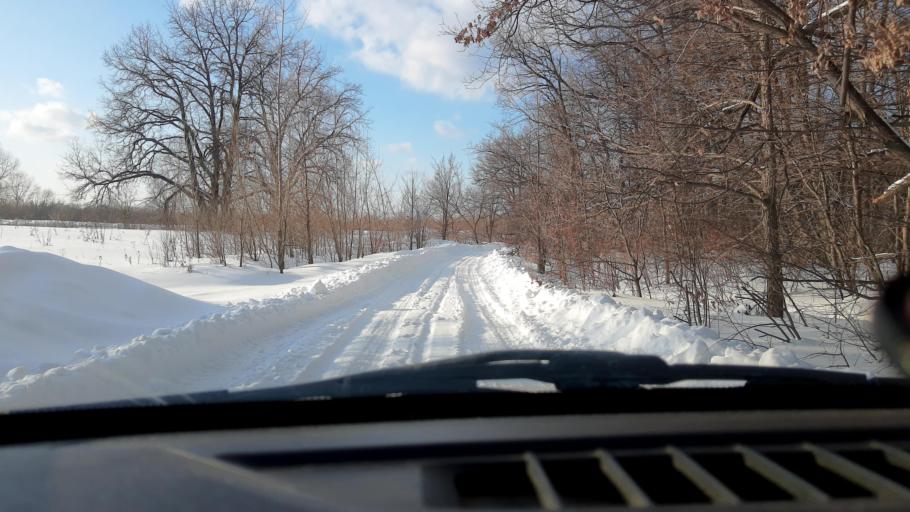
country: RU
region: Bashkortostan
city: Ufa
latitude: 54.6344
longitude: 56.0050
